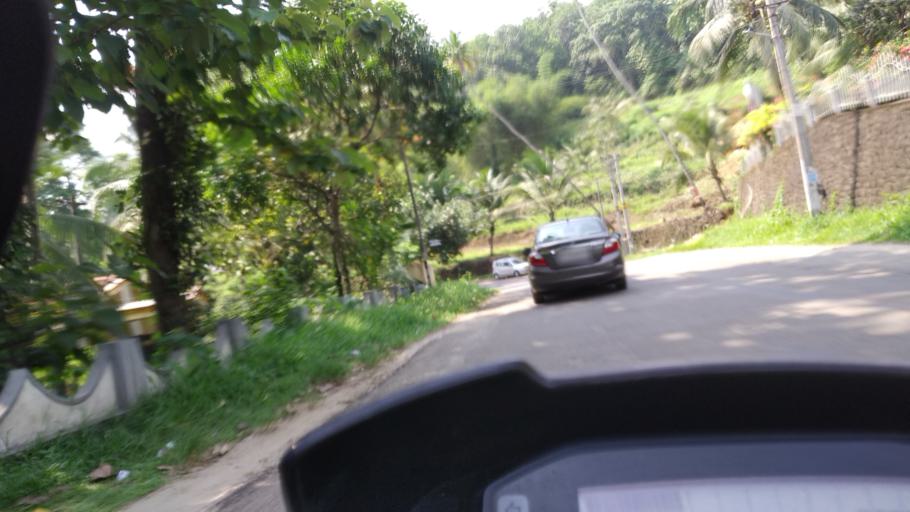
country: IN
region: Kerala
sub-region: Kottayam
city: Erattupetta
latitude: 9.6994
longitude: 76.8105
